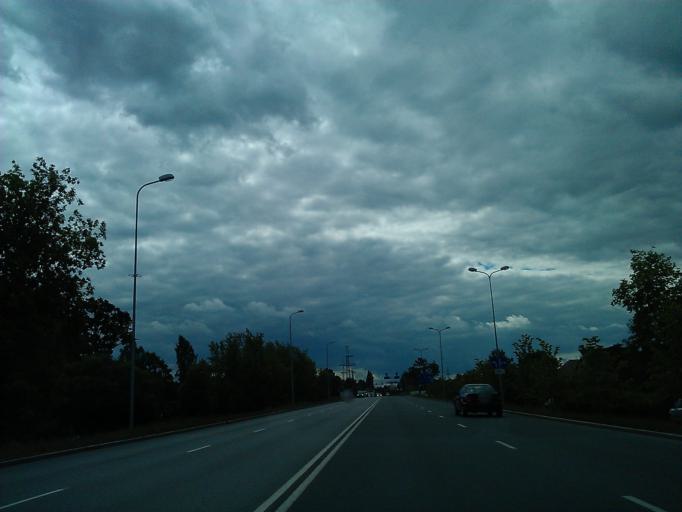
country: LV
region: Jelgava
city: Jelgava
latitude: 56.6334
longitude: 23.7274
